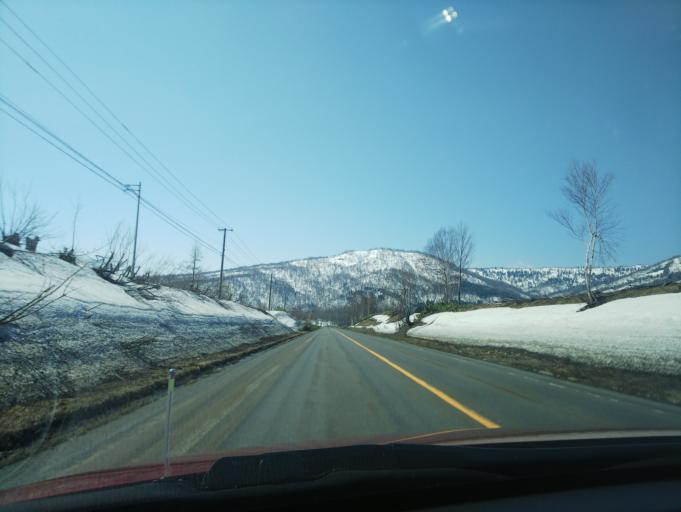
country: JP
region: Hokkaido
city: Nayoro
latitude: 44.6521
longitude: 142.2668
